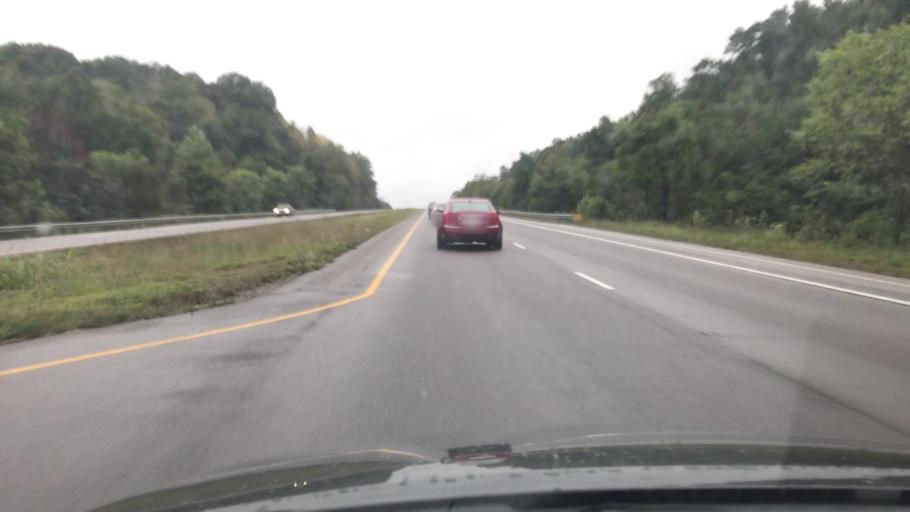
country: US
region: Tennessee
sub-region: Cheatham County
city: Ashland City
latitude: 36.2113
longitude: -86.9565
